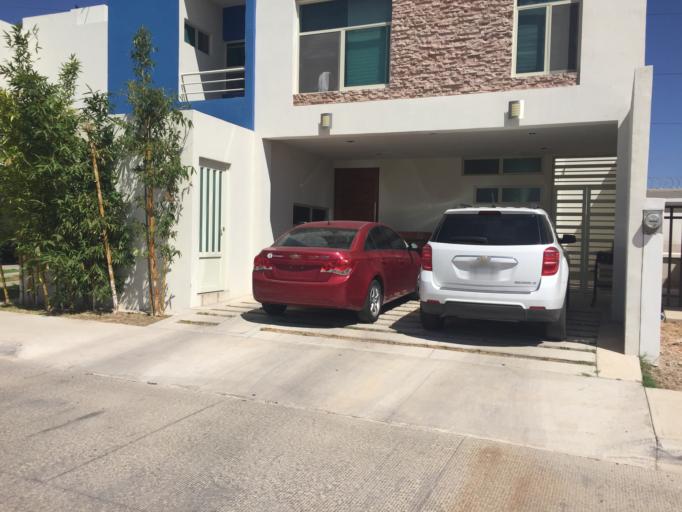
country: MX
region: Durango
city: Victoria de Durango
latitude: 24.0021
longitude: -104.6376
